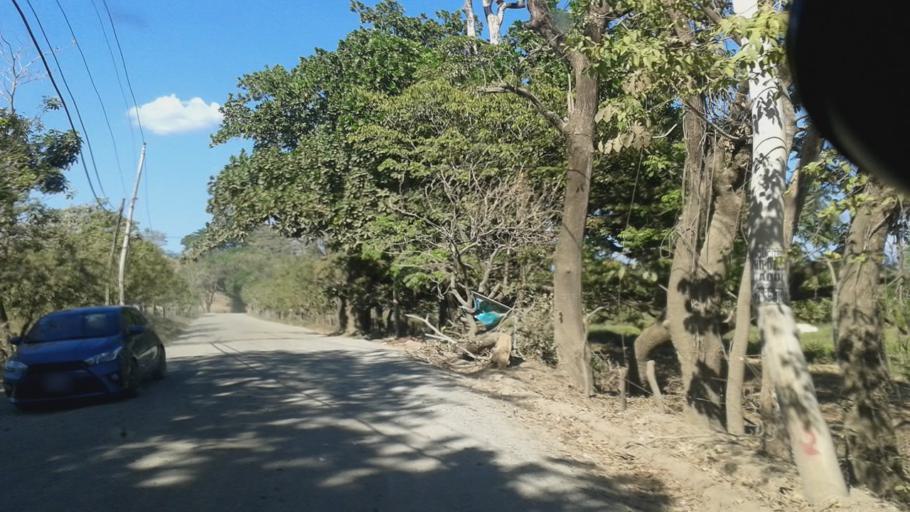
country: CR
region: Guanacaste
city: Samara
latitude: 9.9096
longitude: -85.6405
